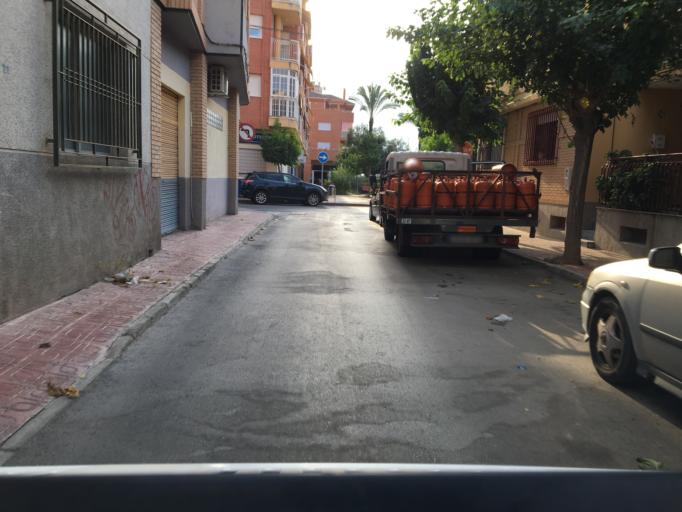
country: ES
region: Murcia
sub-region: Murcia
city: Alcantarilla
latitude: 37.9704
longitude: -1.2078
